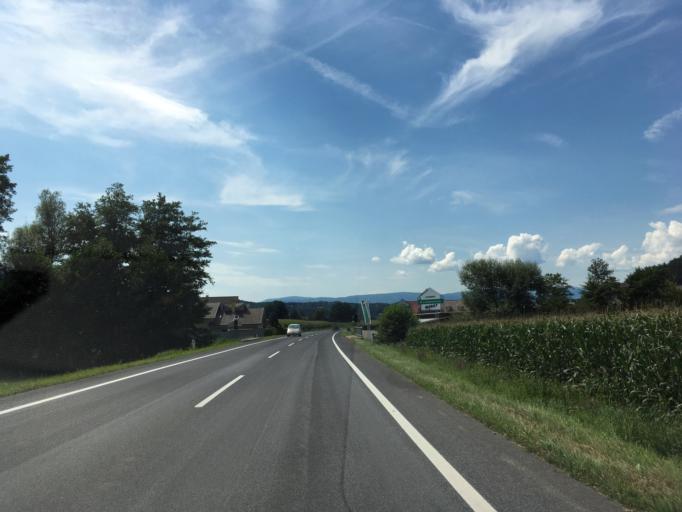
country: AT
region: Styria
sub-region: Politischer Bezirk Leibnitz
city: Oberhaag
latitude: 46.6857
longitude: 15.3590
